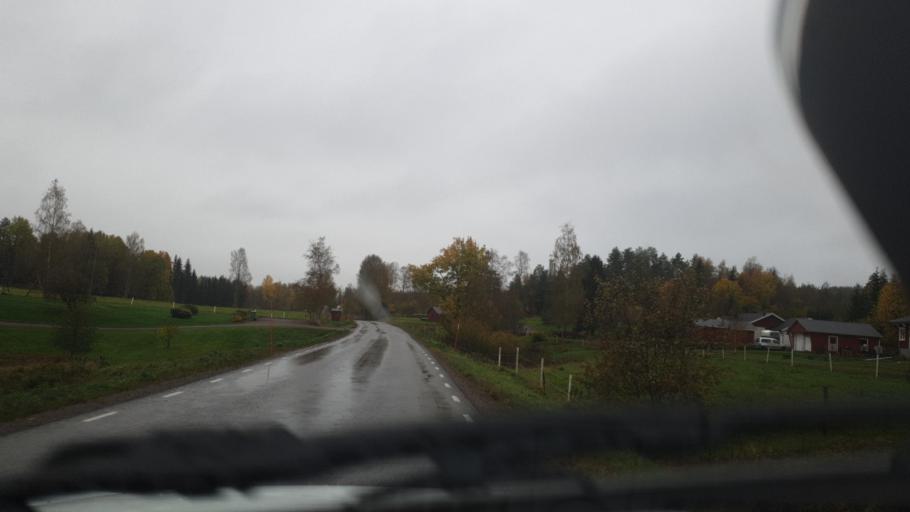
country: SE
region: Vaermland
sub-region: Eda Kommun
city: Charlottenberg
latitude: 59.7955
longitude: 12.1538
